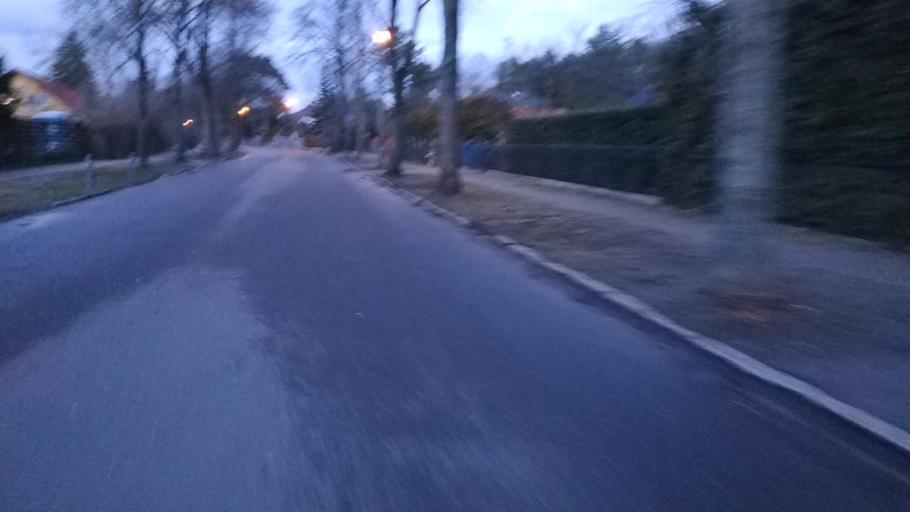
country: DE
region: Brandenburg
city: Petershagen
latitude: 52.5370
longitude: 13.8223
